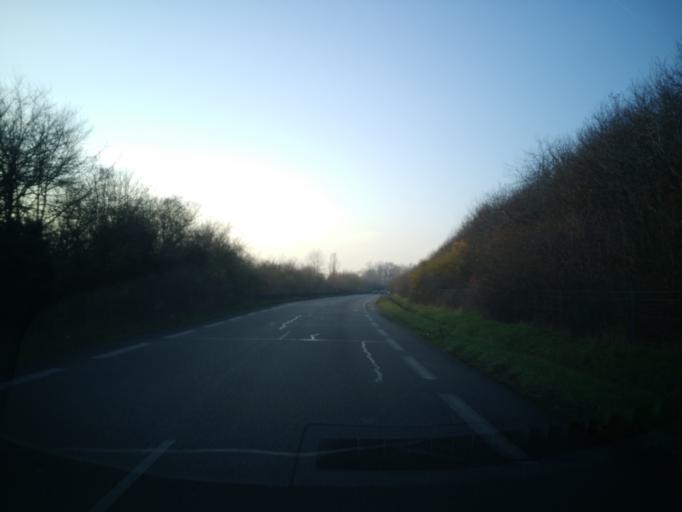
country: FR
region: Ile-de-France
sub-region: Departement des Yvelines
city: Neauphle-le-Chateau
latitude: 48.7993
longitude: 1.9245
